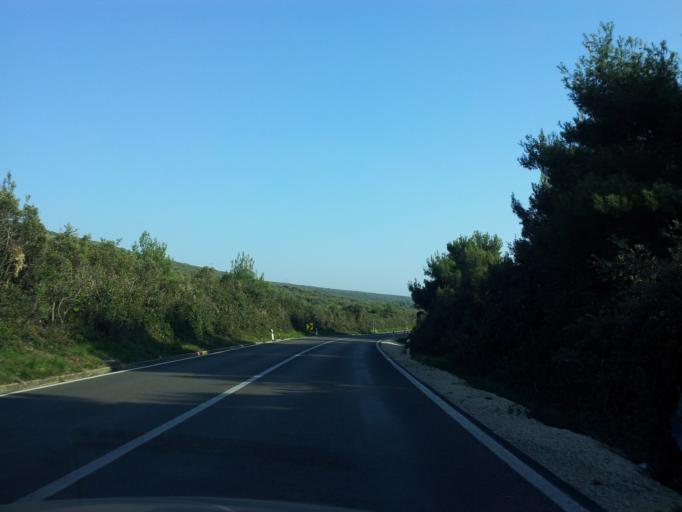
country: HR
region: Zadarska
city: Sukosan
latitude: 44.0197
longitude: 15.3564
